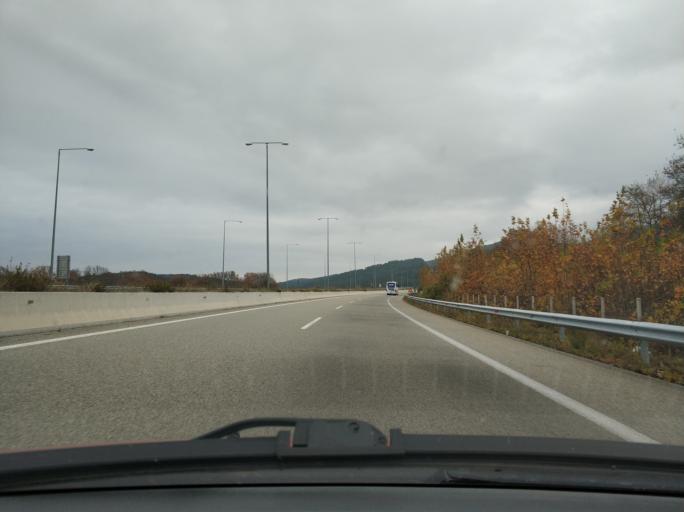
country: GR
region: East Macedonia and Thrace
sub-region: Nomos Kavalas
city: Eleftheroupolis
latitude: 40.8840
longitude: 24.2287
